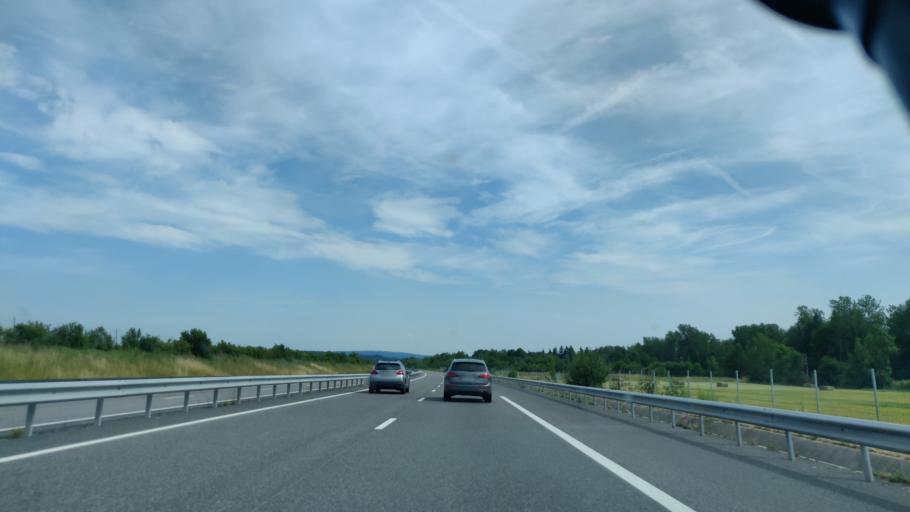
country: FR
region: Lorraine
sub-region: Departement de Meurthe-et-Moselle
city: Baccarat
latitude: 48.4821
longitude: 6.7124
